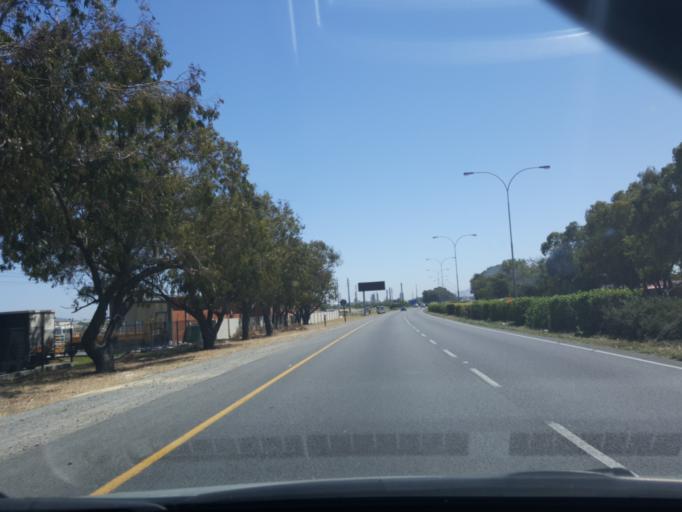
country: ZA
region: Western Cape
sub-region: City of Cape Town
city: Sunset Beach
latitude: -33.8669
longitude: 18.5294
